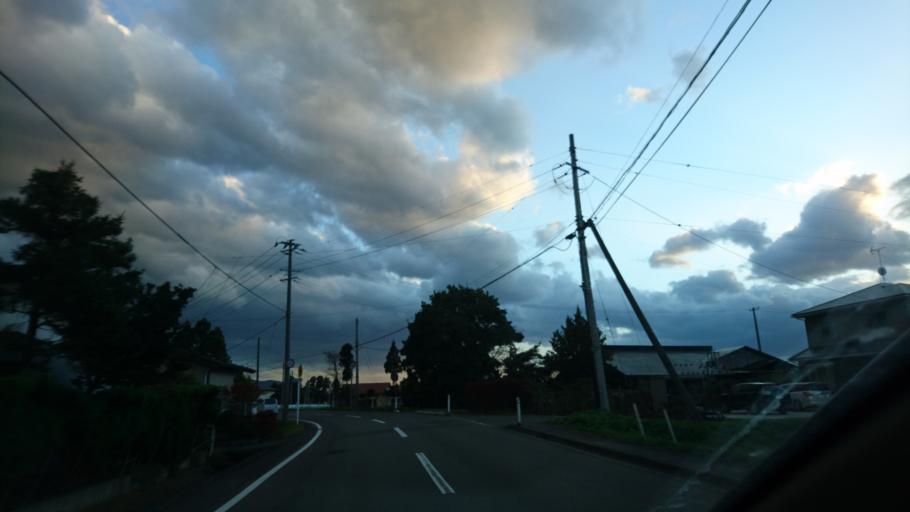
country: JP
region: Iwate
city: Mizusawa
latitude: 39.1123
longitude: 141.1503
